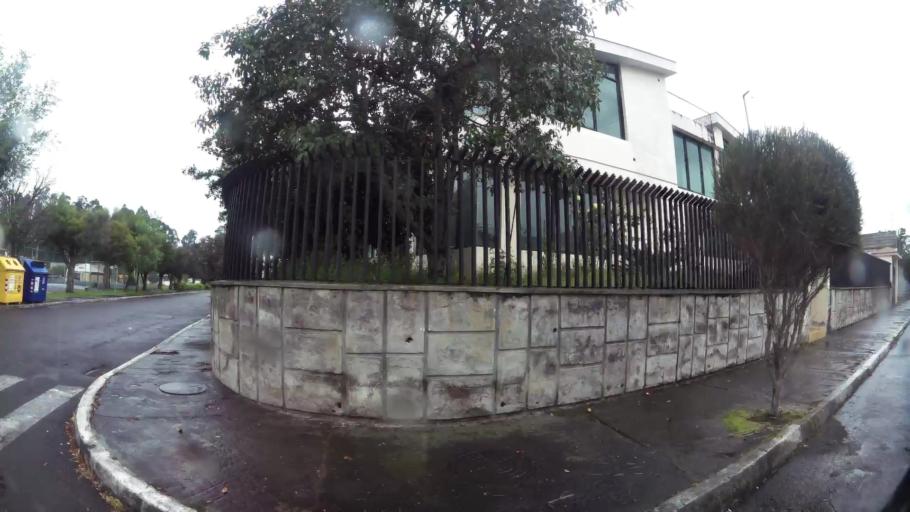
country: EC
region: Pichincha
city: Sangolqui
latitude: -0.3130
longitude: -78.4412
